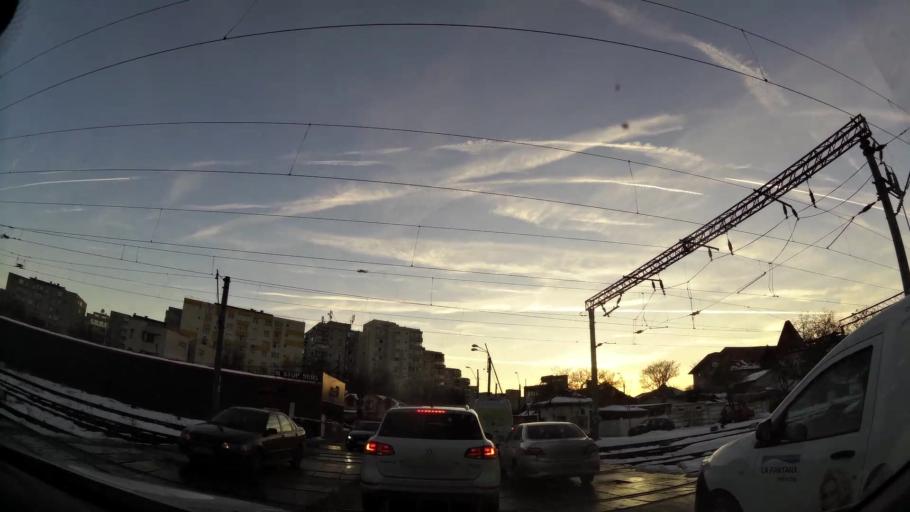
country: RO
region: Ilfov
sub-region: Comuna Fundeni-Dobroesti
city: Fundeni
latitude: 44.4474
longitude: 26.1449
